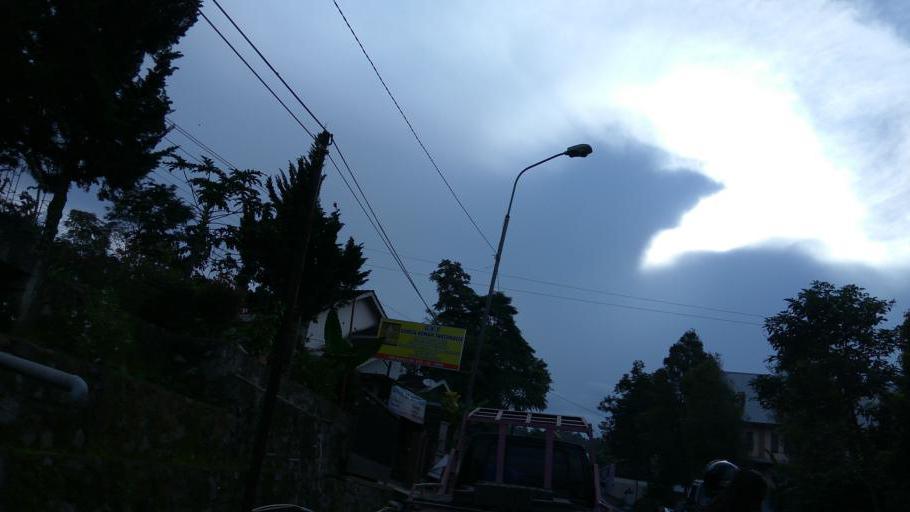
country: ID
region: Central Java
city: Gunung Kendil
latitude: -7.3716
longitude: 110.4478
